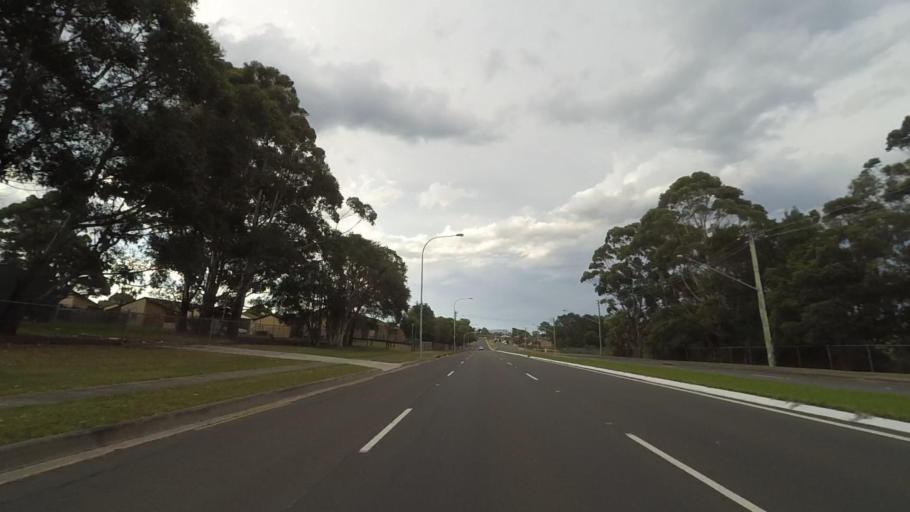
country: AU
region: New South Wales
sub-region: Shellharbour
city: Barrack Heights
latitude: -34.5708
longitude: 150.8621
